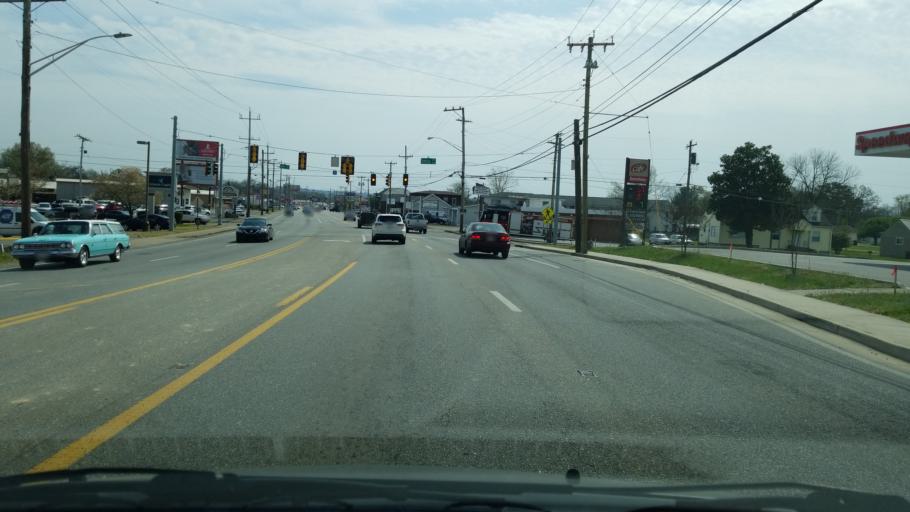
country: US
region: Tennessee
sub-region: Hamilton County
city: East Ridge
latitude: 34.9966
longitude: -85.2415
